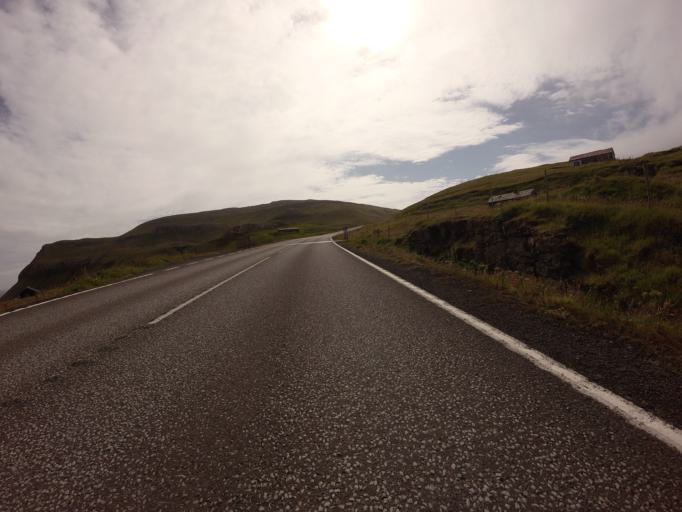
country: FO
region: Sandoy
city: Sandur
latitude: 61.8961
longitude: -6.8684
